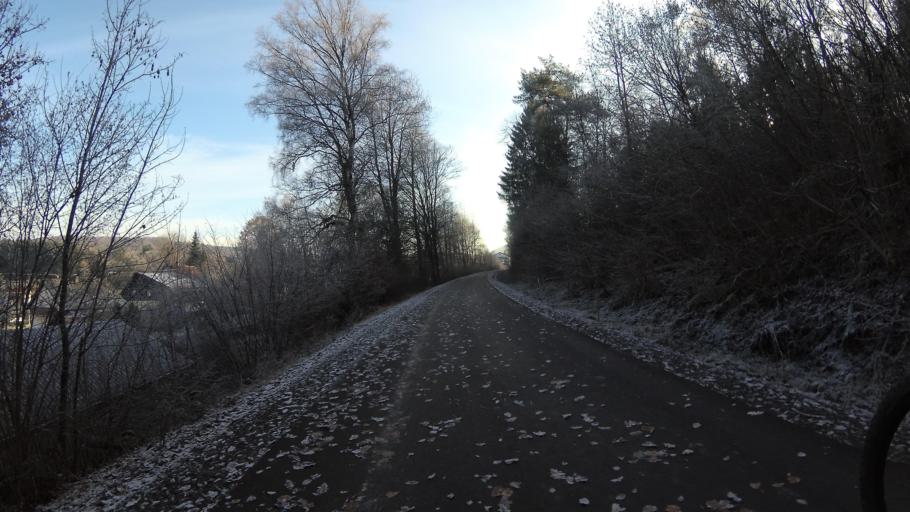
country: DE
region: Saarland
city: Nohfelden
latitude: 49.5825
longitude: 7.1407
